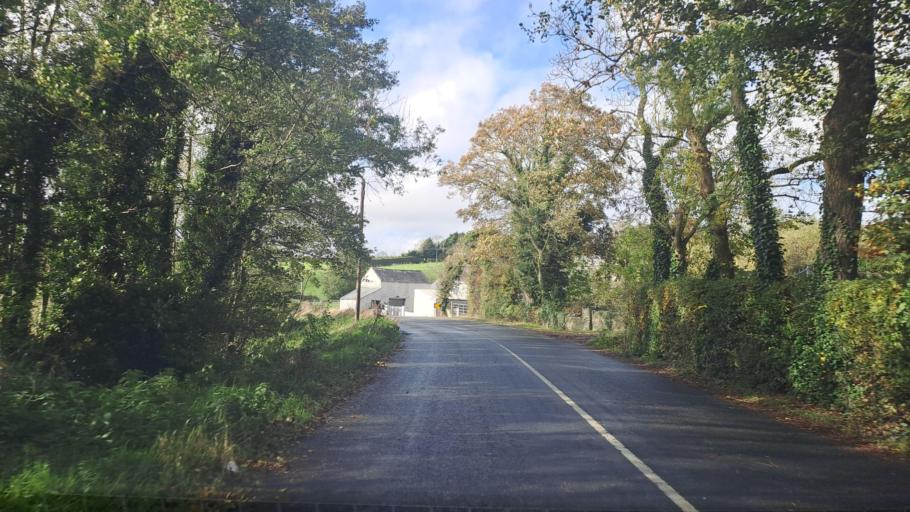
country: IE
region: Ulster
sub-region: An Cabhan
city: Cootehill
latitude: 54.1095
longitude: -6.9662
